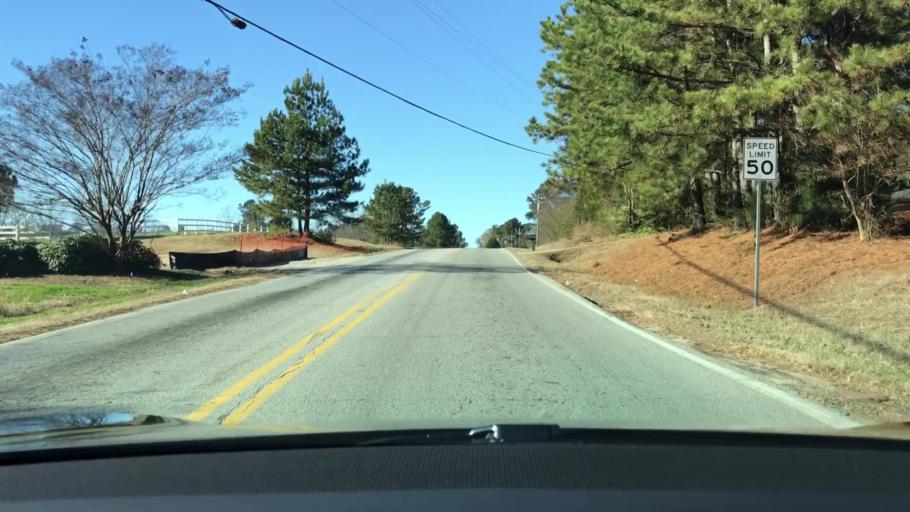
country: US
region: Georgia
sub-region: Barrow County
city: Auburn
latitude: 33.9740
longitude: -83.7868
